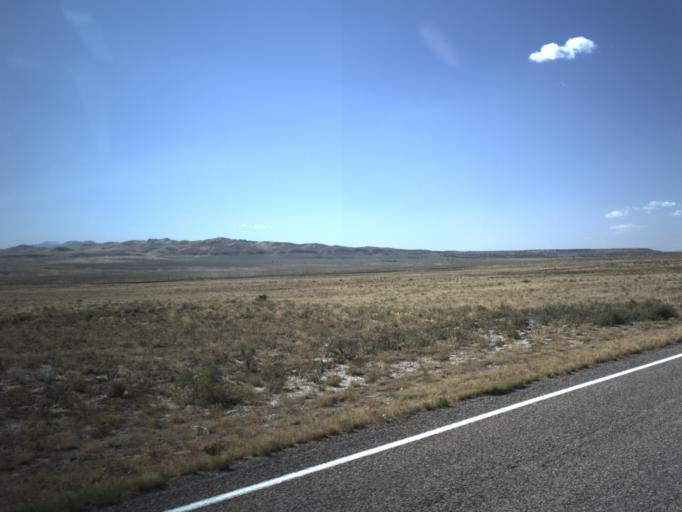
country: US
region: Utah
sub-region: Beaver County
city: Milford
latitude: 38.8185
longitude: -112.8601
